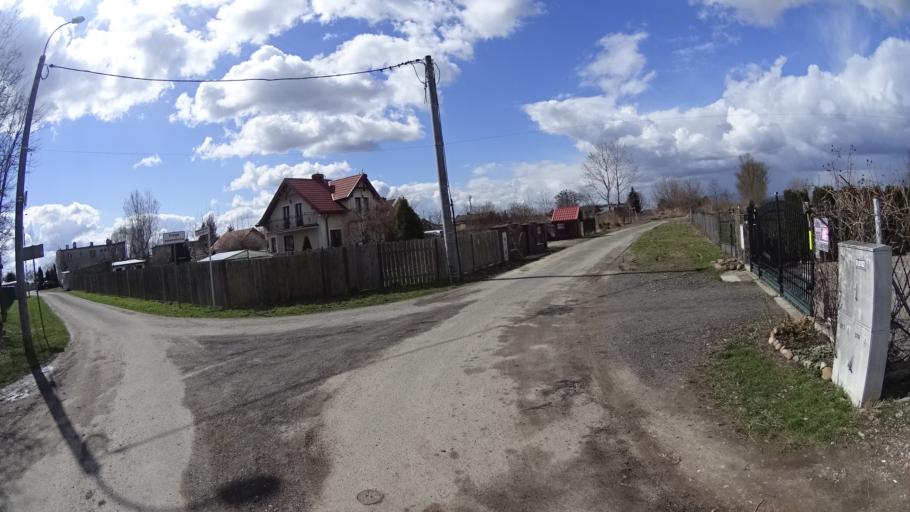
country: PL
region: Masovian Voivodeship
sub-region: Powiat warszawski zachodni
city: Jozefow
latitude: 52.2169
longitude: 20.7181
